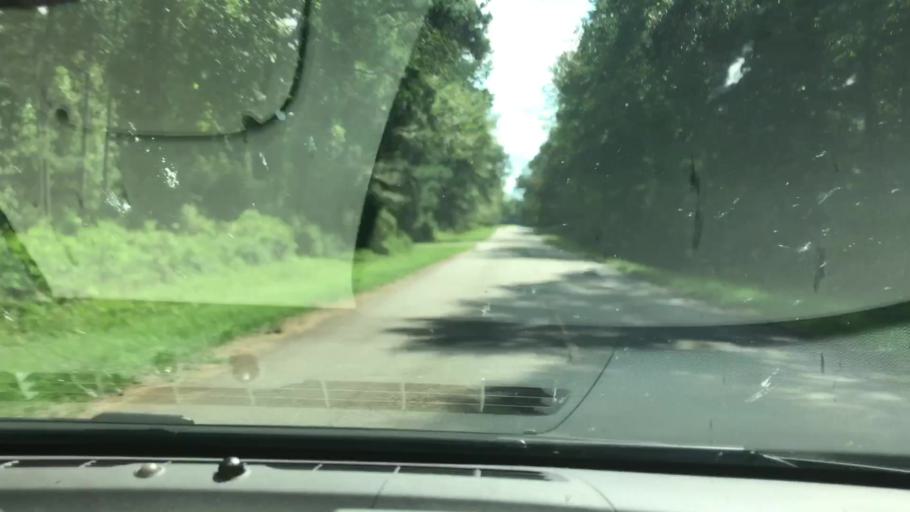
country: US
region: Georgia
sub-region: Troup County
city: La Grange
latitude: 33.1050
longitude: -85.1287
